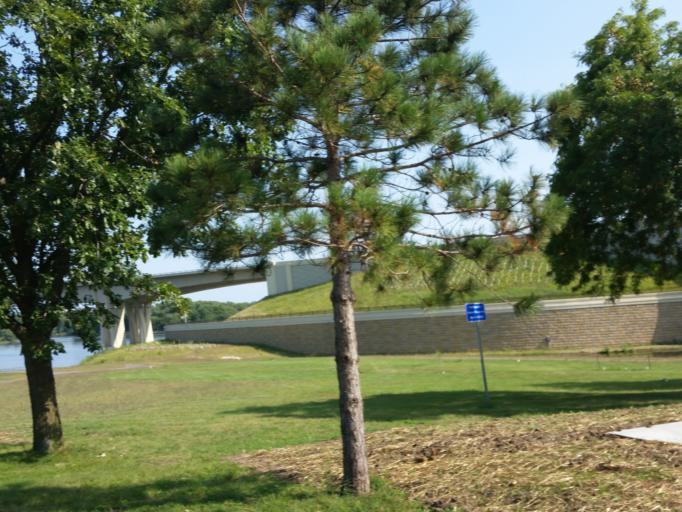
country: US
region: Minnesota
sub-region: Houston County
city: La Crescent
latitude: 43.8595
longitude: -91.3042
